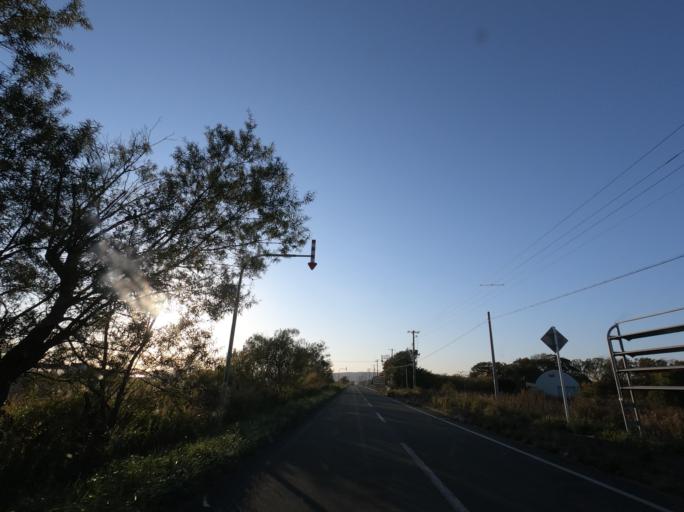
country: JP
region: Hokkaido
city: Iwamizawa
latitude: 42.9793
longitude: 141.8467
